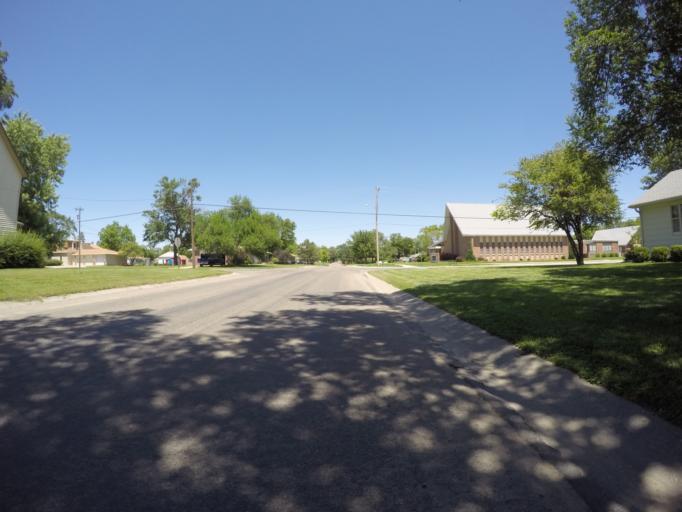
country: US
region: Kansas
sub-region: Republic County
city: Belleville
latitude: 39.8182
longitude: -97.6282
